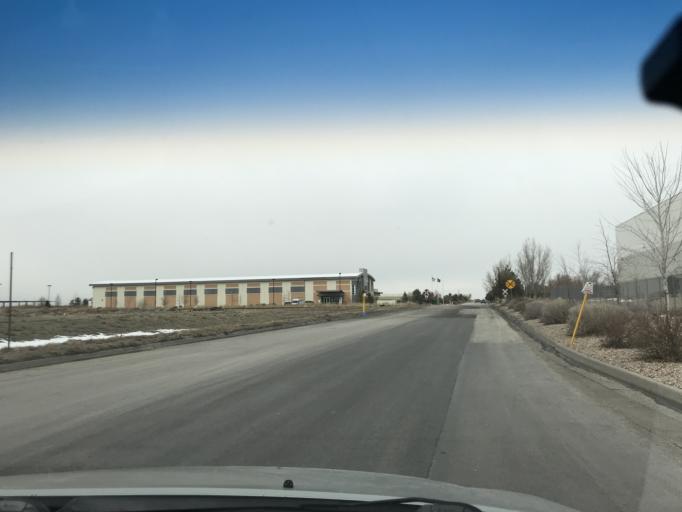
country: US
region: Utah
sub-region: Salt Lake County
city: West Valley City
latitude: 40.7790
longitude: -112.0362
